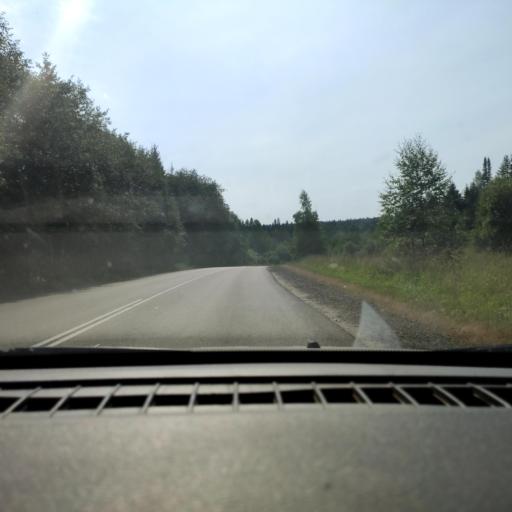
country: RU
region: Perm
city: Novyye Lyady
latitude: 58.1232
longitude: 56.4634
